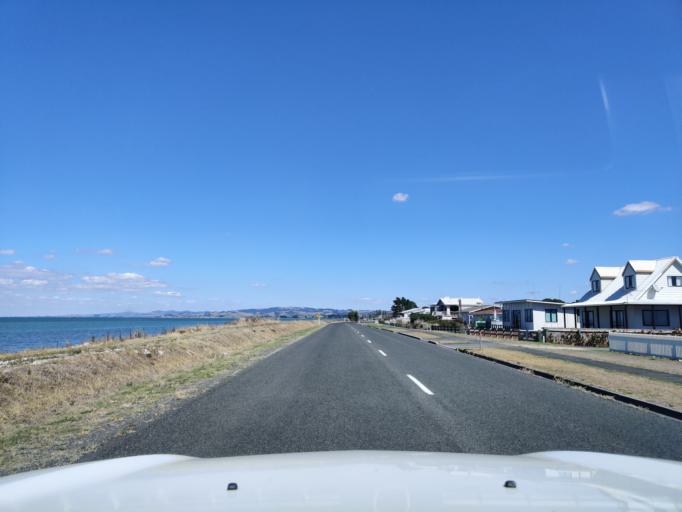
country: NZ
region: Waikato
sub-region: Thames-Coromandel District
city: Thames
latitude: -37.1071
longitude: 175.2992
